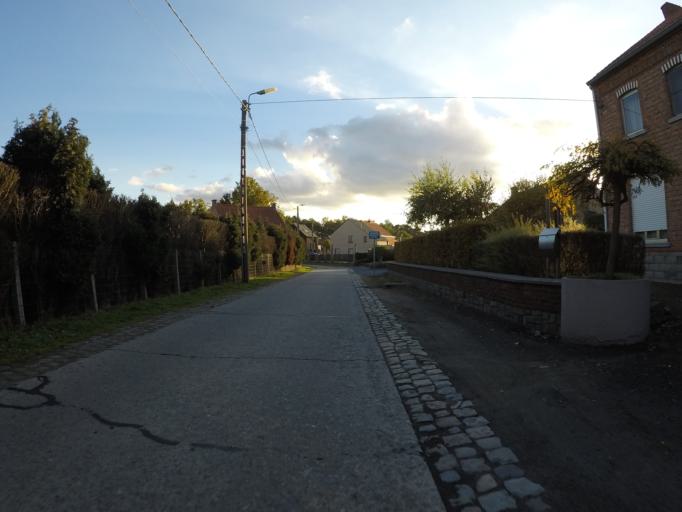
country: BE
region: Flanders
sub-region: Provincie Vlaams-Brabant
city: Begijnendijk
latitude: 50.9956
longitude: 4.8048
